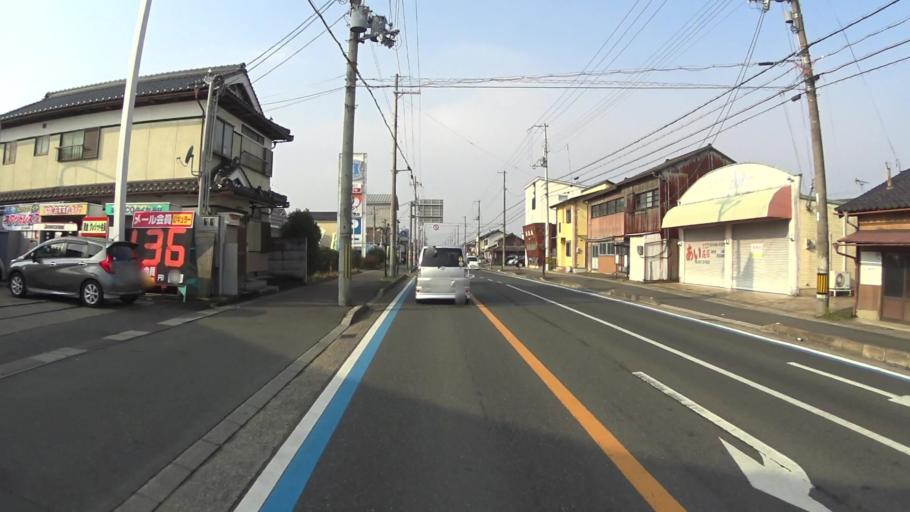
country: JP
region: Kyoto
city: Fukuchiyama
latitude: 35.2975
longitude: 135.1596
